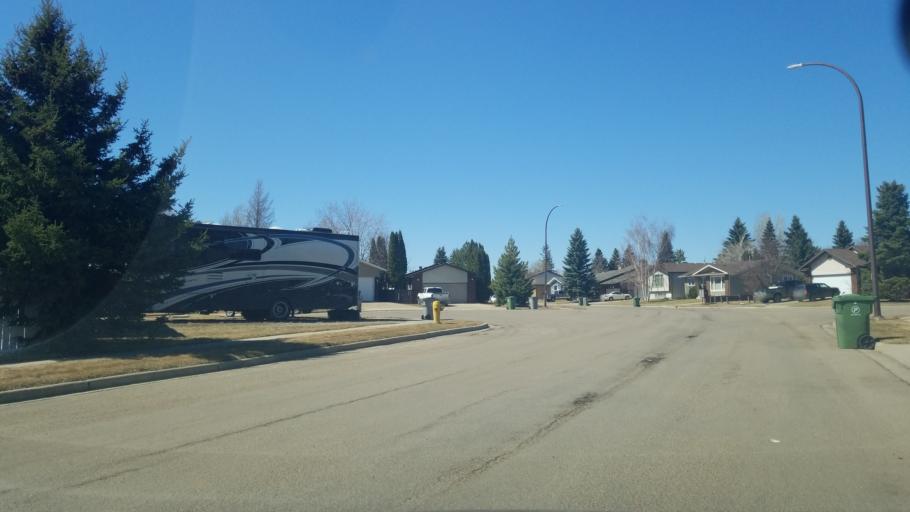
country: CA
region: Saskatchewan
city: Lloydminster
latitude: 53.2627
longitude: -110.0167
